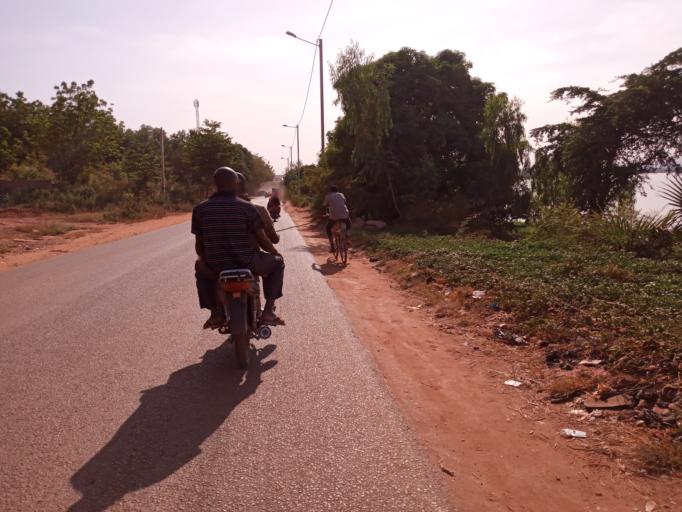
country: ML
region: Bamako
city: Bamako
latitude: 12.6288
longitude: -7.9531
